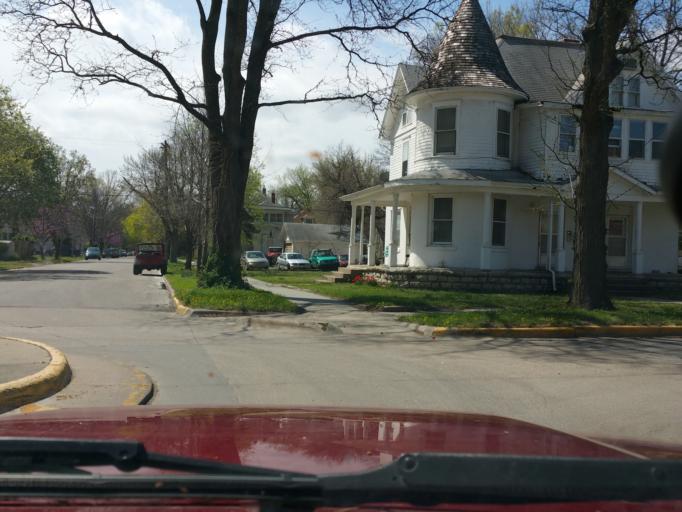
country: US
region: Kansas
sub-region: Riley County
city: Manhattan
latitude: 39.1857
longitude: -96.5683
